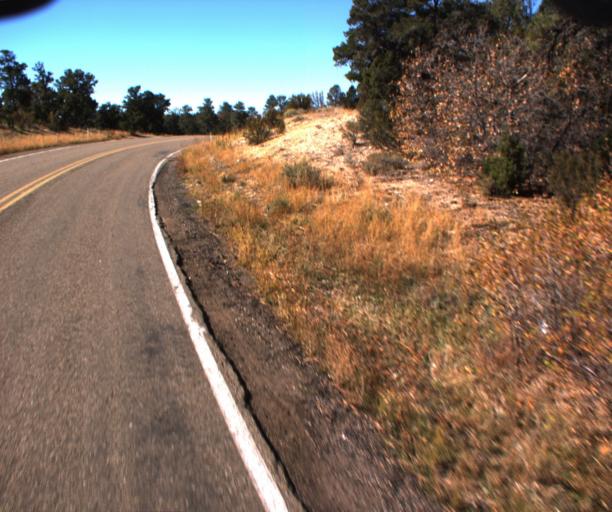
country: US
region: Arizona
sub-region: Coconino County
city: Fredonia
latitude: 36.7921
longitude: -112.2554
